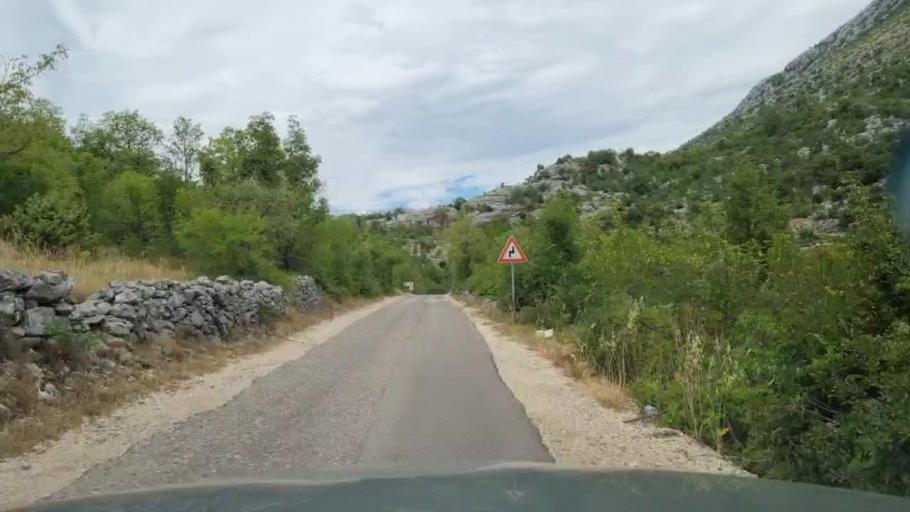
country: HR
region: Dubrovacko-Neretvanska
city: Podgora
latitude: 42.9649
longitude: 17.7957
